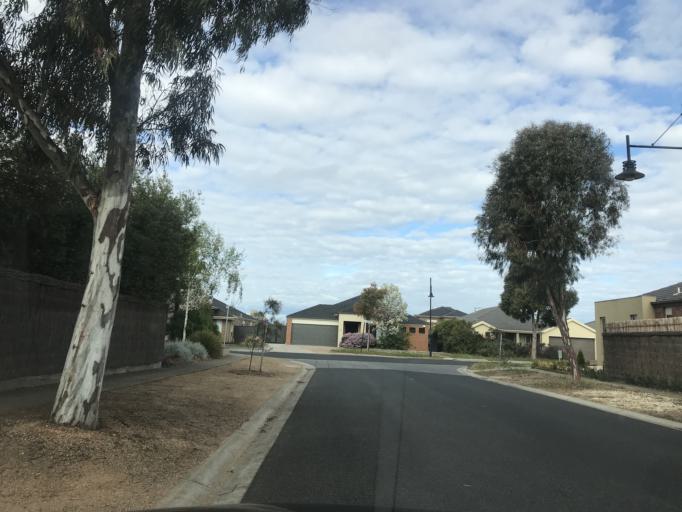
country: AU
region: Victoria
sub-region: Wyndham
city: Williams Landing
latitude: -37.8868
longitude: 144.7377
